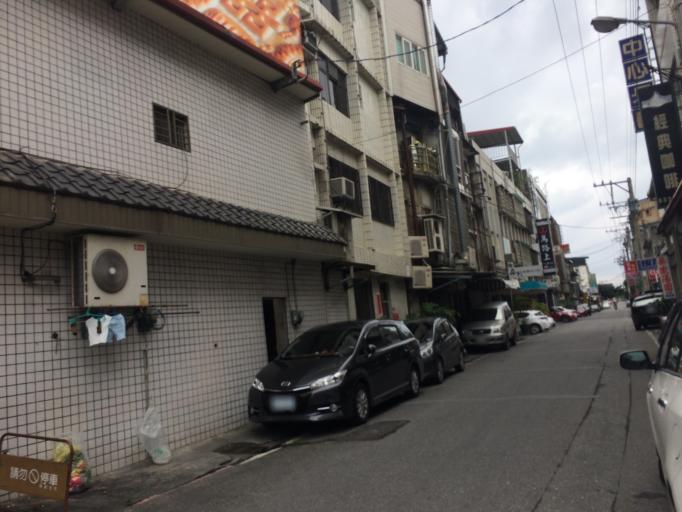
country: TW
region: Taiwan
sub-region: Hualien
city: Hualian
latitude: 23.9760
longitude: 121.6082
